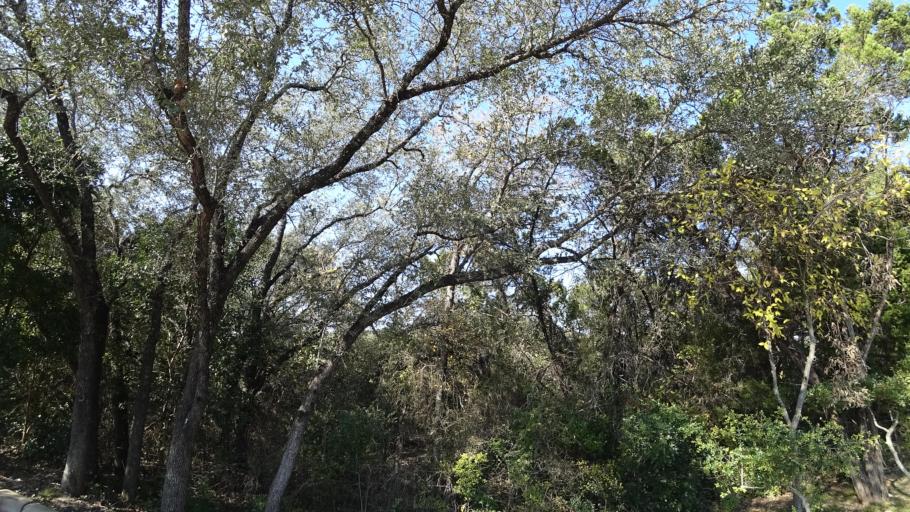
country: US
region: Texas
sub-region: Williamson County
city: Jollyville
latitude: 30.3849
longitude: -97.7694
